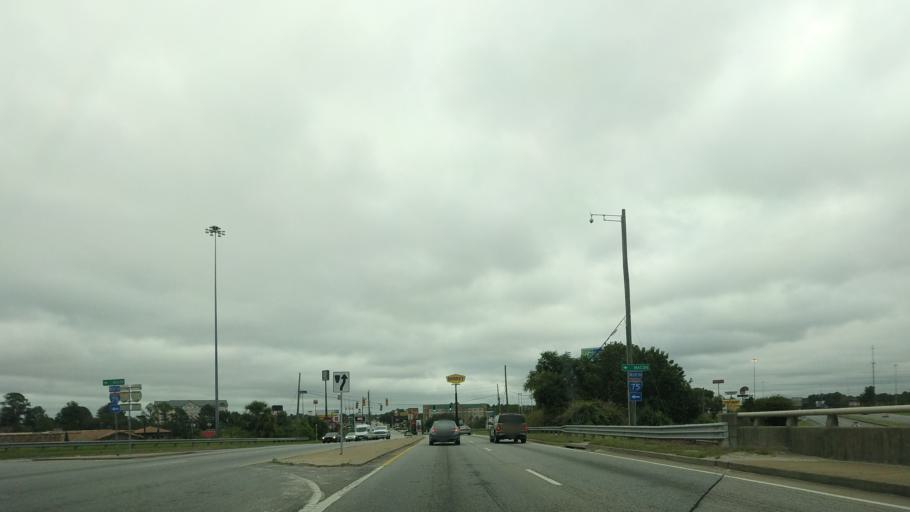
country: US
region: Georgia
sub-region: Lowndes County
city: Remerton
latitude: 30.8445
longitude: -83.3302
